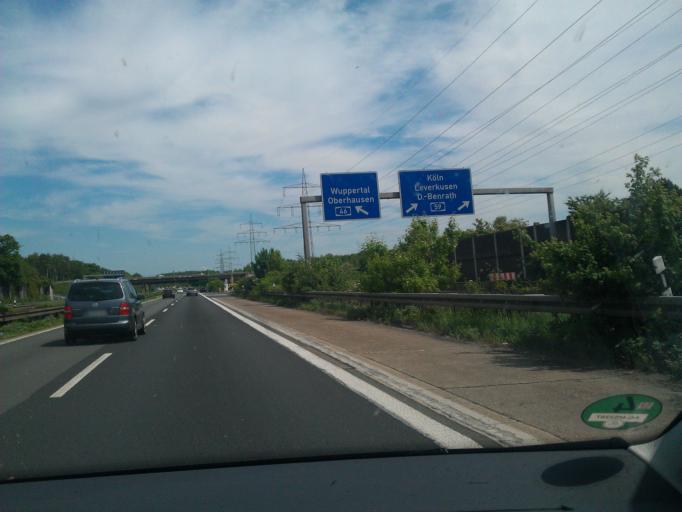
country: DE
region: North Rhine-Westphalia
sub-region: Regierungsbezirk Dusseldorf
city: Erkrath
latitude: 51.1900
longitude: 6.8631
